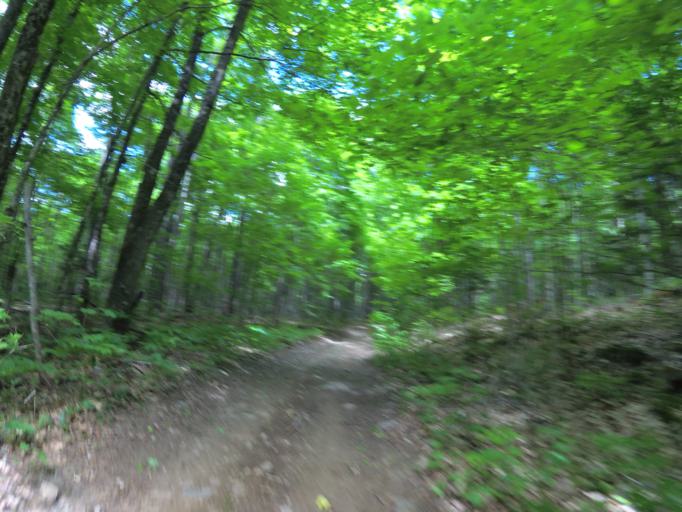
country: CA
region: Ontario
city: Renfrew
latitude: 45.0545
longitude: -76.8611
